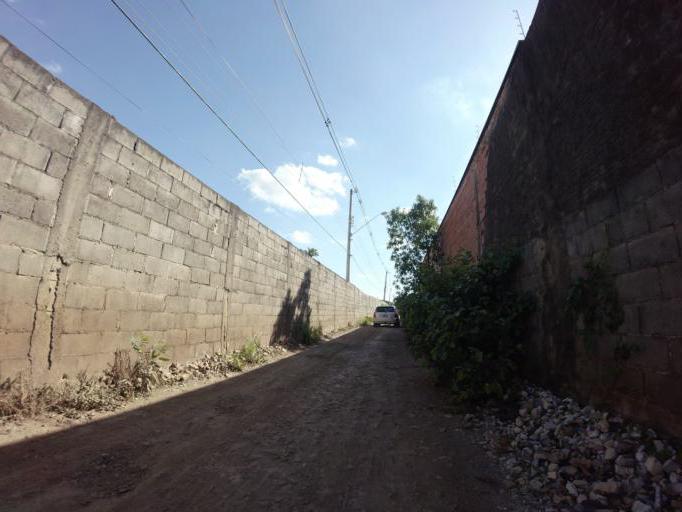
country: BR
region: Sao Paulo
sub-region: Piracicaba
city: Piracicaba
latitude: -22.7353
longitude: -47.5997
